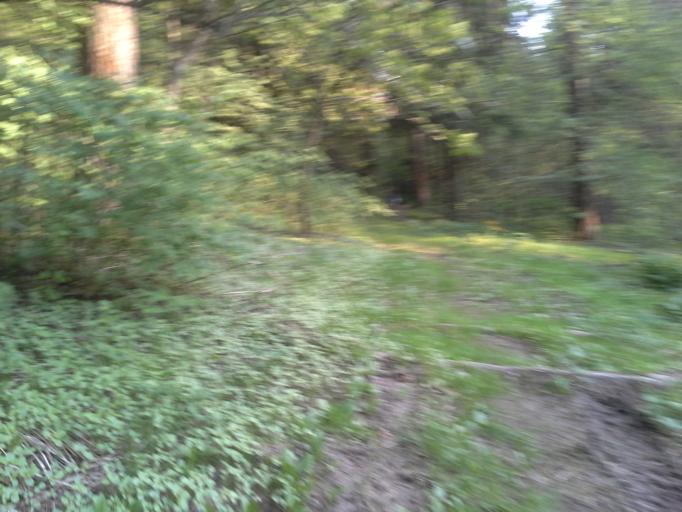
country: RU
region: Moscow
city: Novo-Peredelkino
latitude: 55.6451
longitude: 37.3072
